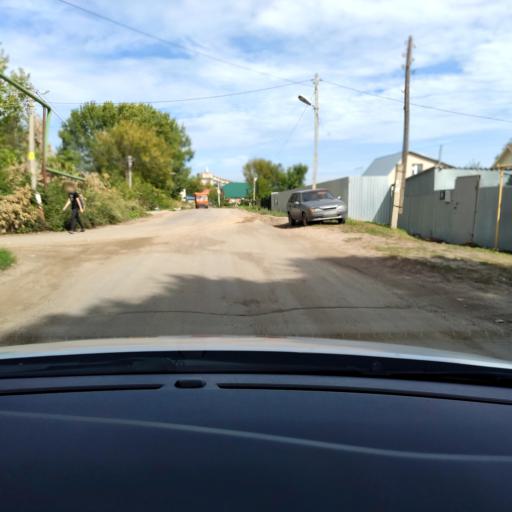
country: RU
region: Tatarstan
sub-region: Gorod Kazan'
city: Kazan
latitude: 55.7168
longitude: 49.0913
